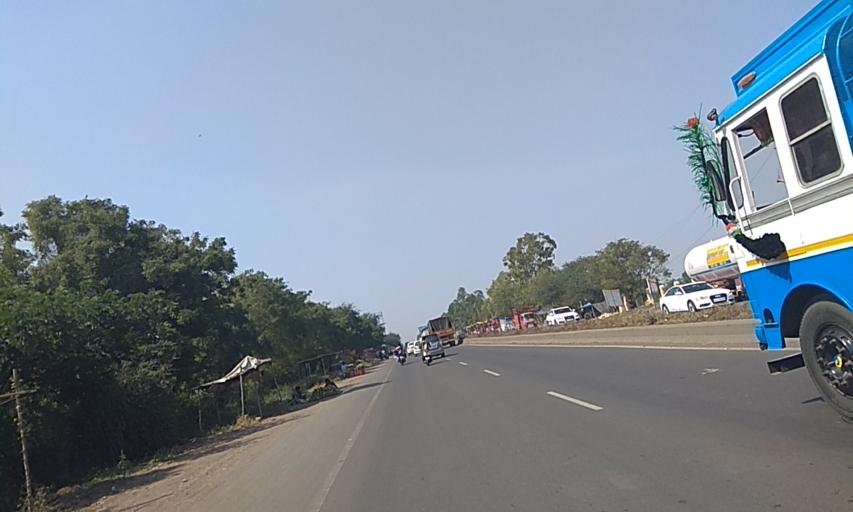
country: IN
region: Maharashtra
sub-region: Pune Division
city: Lohogaon
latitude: 18.4941
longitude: 73.9862
